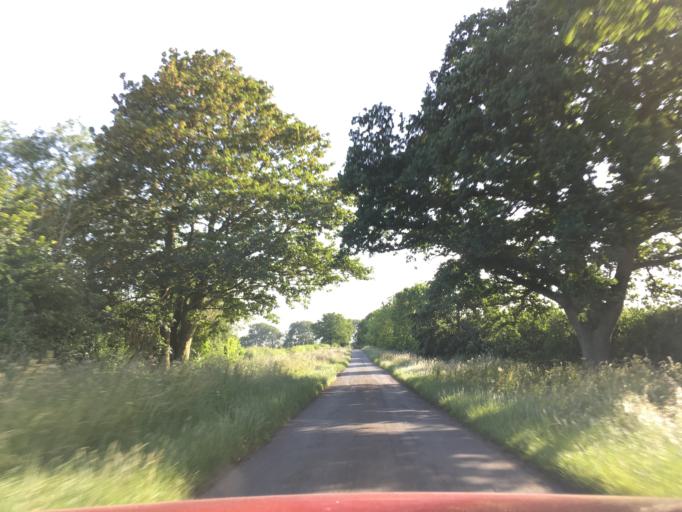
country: GB
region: England
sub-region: Gloucestershire
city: Fairford
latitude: 51.7294
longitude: -1.7524
